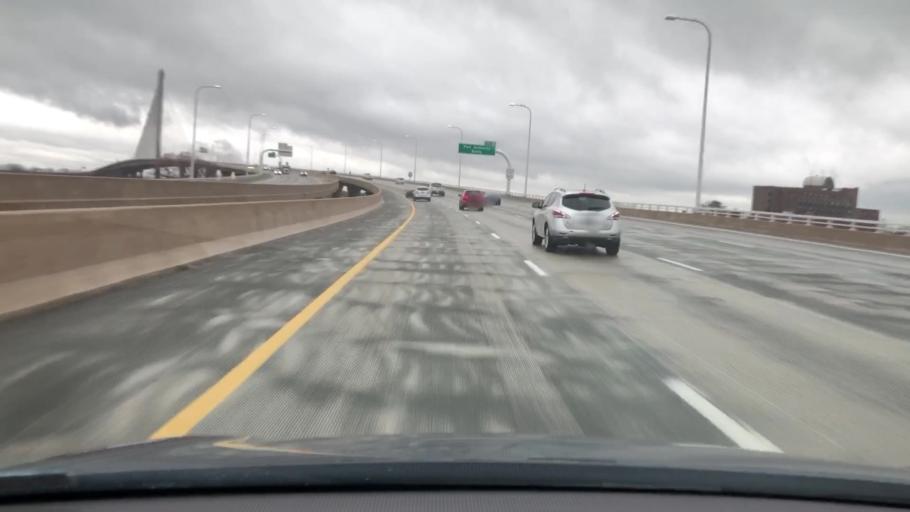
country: US
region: Ohio
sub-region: Lucas County
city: Oregon
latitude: 41.6675
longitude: -83.5150
